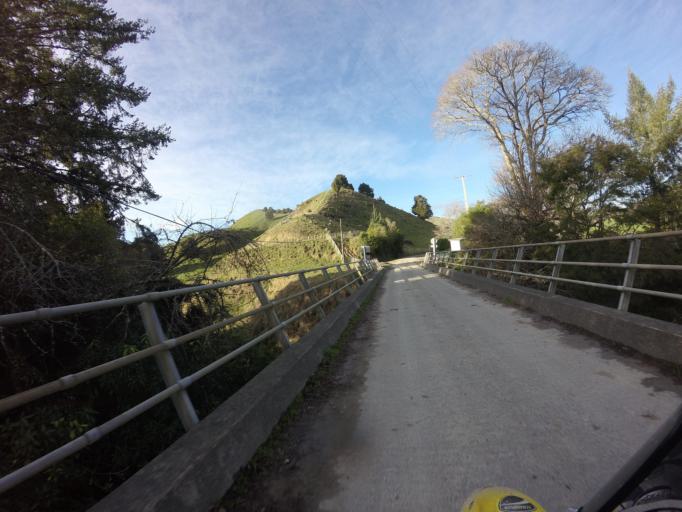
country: NZ
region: Hawke's Bay
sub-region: Wairoa District
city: Wairoa
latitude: -38.7172
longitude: 177.5533
